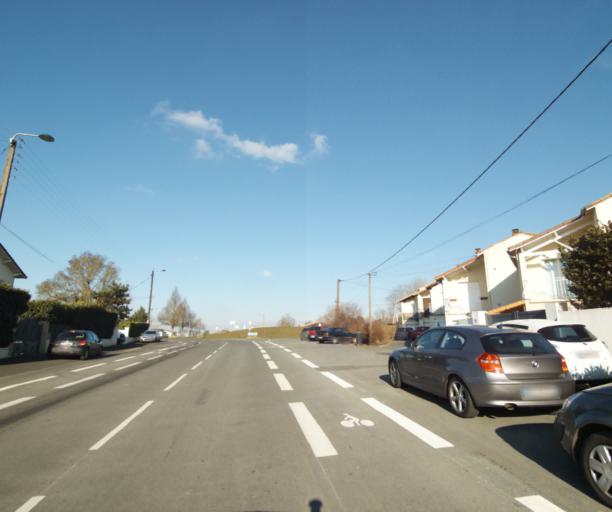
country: FR
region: Poitou-Charentes
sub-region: Departement des Deux-Sevres
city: Niort
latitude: 46.3426
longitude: -0.4544
